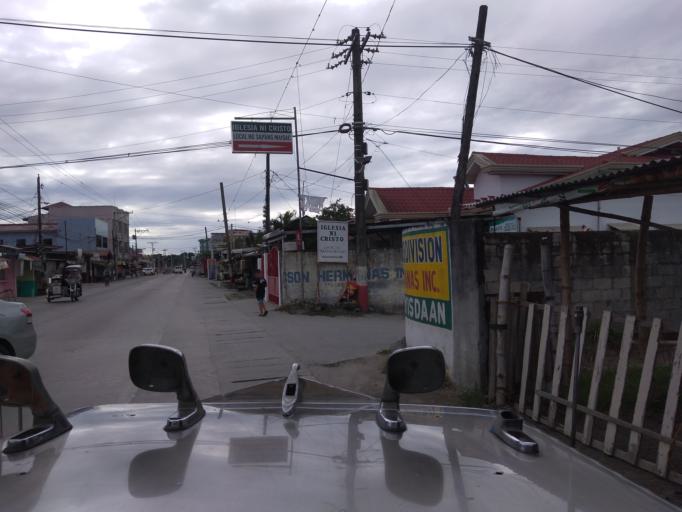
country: PH
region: Central Luzon
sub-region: Province of Pampanga
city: Pandacaqui
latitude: 15.1802
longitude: 120.6268
